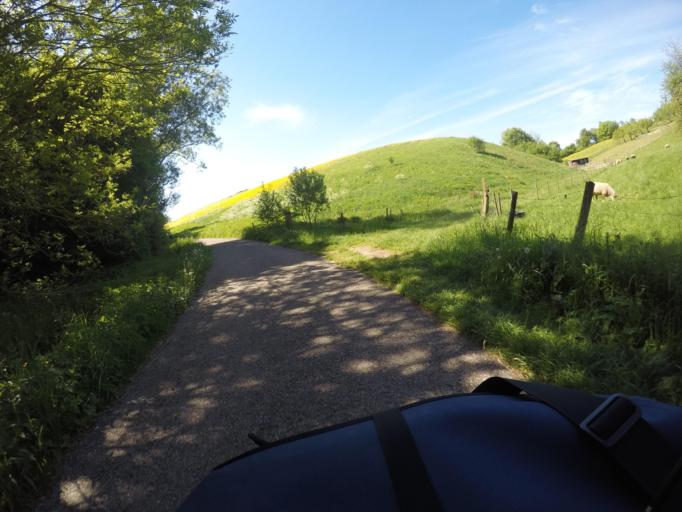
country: DE
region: Baden-Wuerttemberg
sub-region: Regierungsbezirk Stuttgart
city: Huttlingen
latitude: 48.8681
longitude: 10.0844
